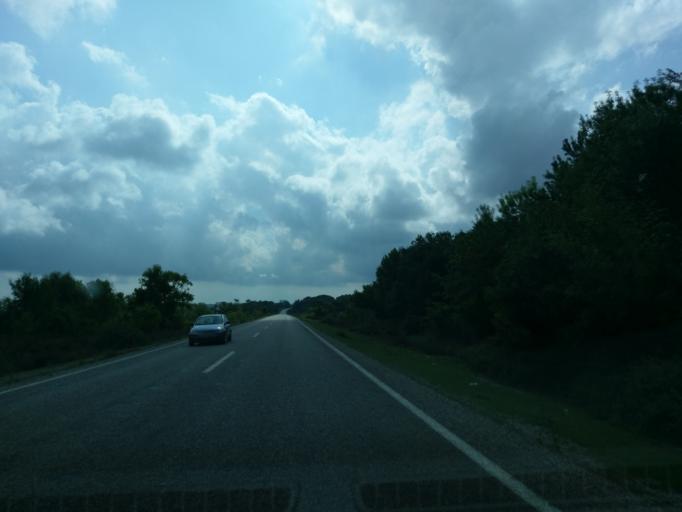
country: TR
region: Sinop
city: Sinop
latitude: 42.0268
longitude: 35.0386
